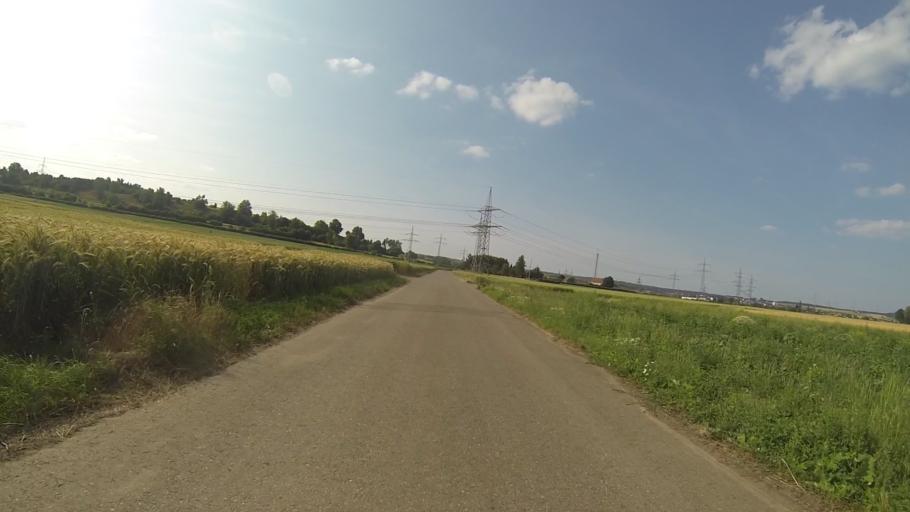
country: DE
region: Baden-Wuerttemberg
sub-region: Regierungsbezirk Stuttgart
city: Niederstotzingen
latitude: 48.5226
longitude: 10.2310
